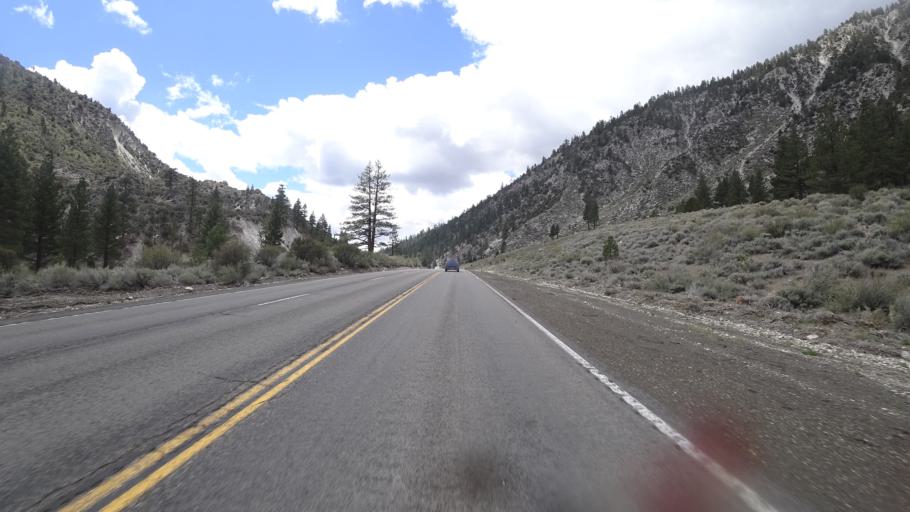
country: US
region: California
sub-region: Mono County
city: Bridgeport
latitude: 38.4076
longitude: -119.4517
